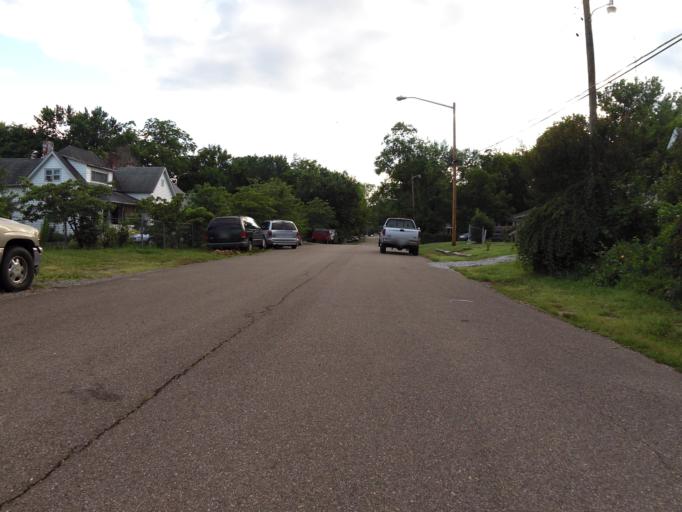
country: US
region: Tennessee
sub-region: Knox County
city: Knoxville
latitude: 36.0015
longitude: -83.9338
